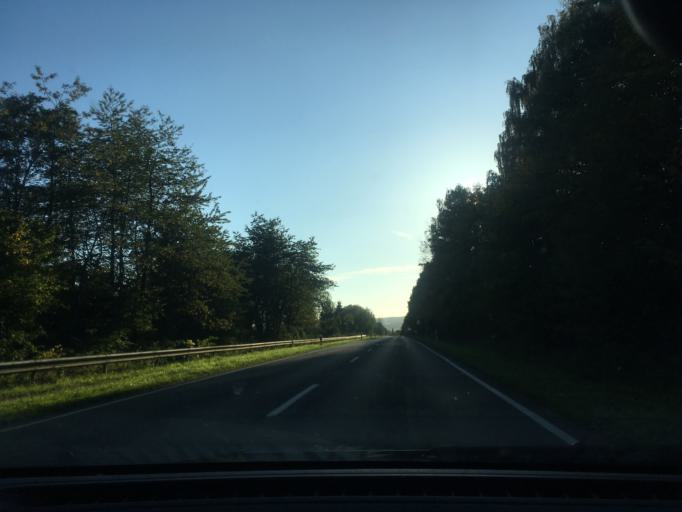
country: DE
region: Lower Saxony
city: Dassel
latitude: 51.8037
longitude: 9.7150
